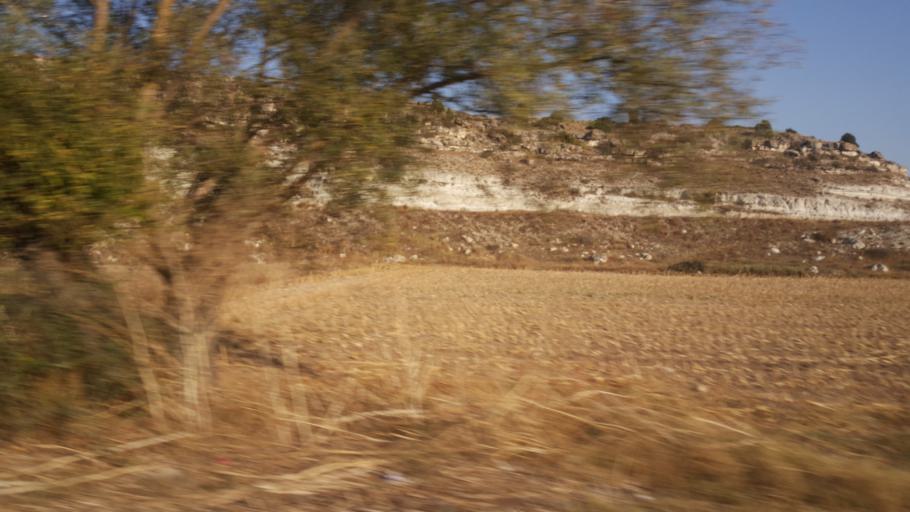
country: TR
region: Eskisehir
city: Seyitgazi
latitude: 39.4194
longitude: 30.6512
